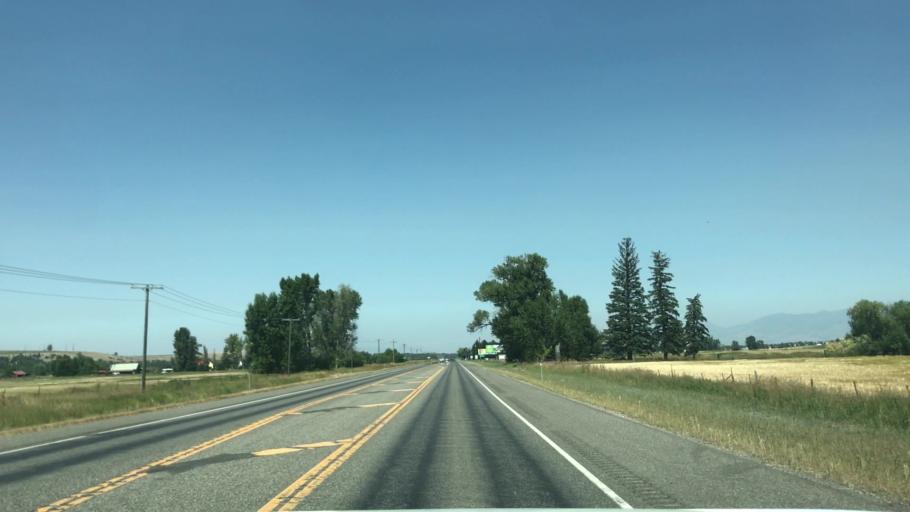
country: US
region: Montana
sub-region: Gallatin County
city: Four Corners
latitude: 45.6203
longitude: -111.1969
